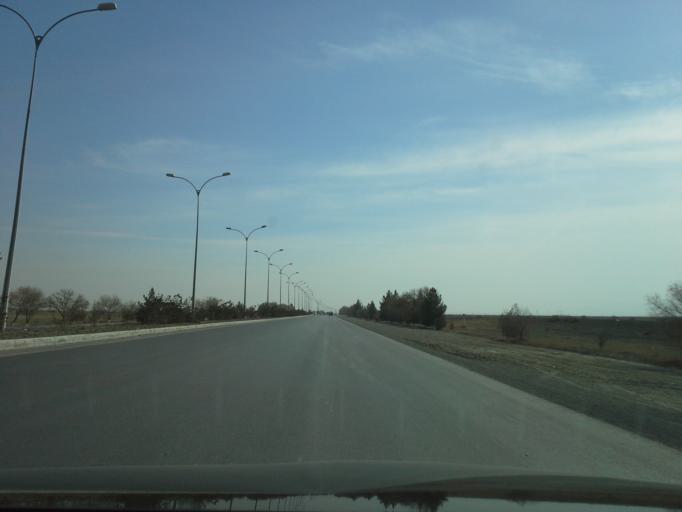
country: TM
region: Ahal
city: Abadan
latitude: 38.1272
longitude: 58.0297
